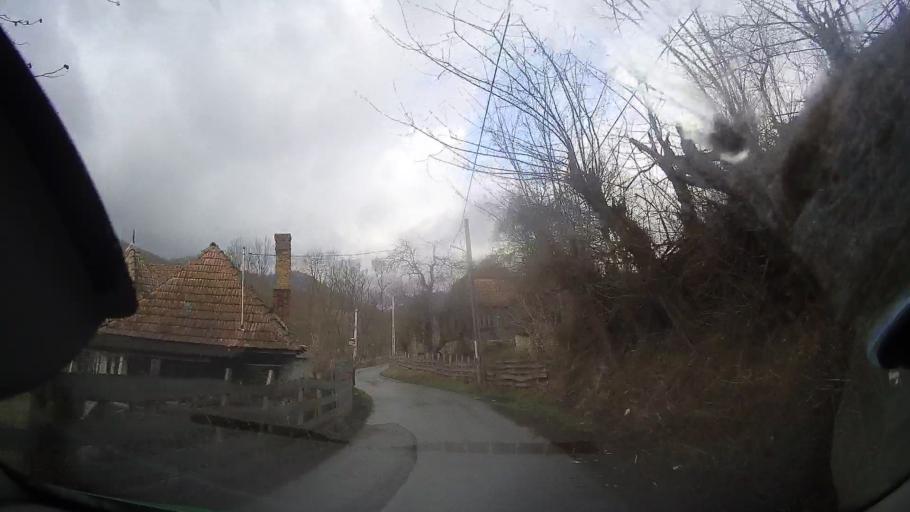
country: RO
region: Alba
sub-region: Comuna Ocolis
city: Ocolis
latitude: 46.4898
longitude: 23.4587
